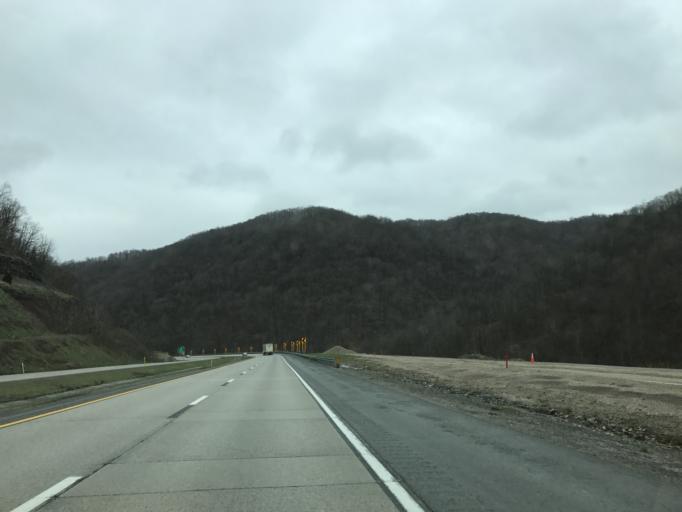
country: US
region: West Virginia
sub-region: Summers County
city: Hinton
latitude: 37.7795
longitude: -80.9333
